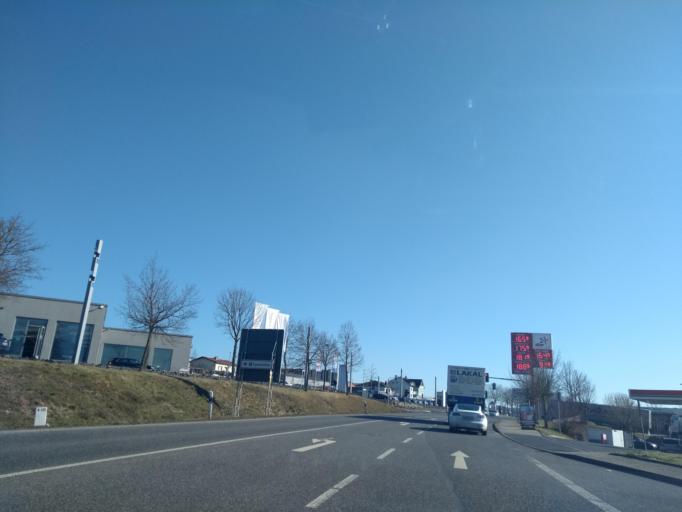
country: DE
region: Hesse
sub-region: Regierungsbezirk Kassel
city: Hunfeld
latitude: 50.6890
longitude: 9.7537
